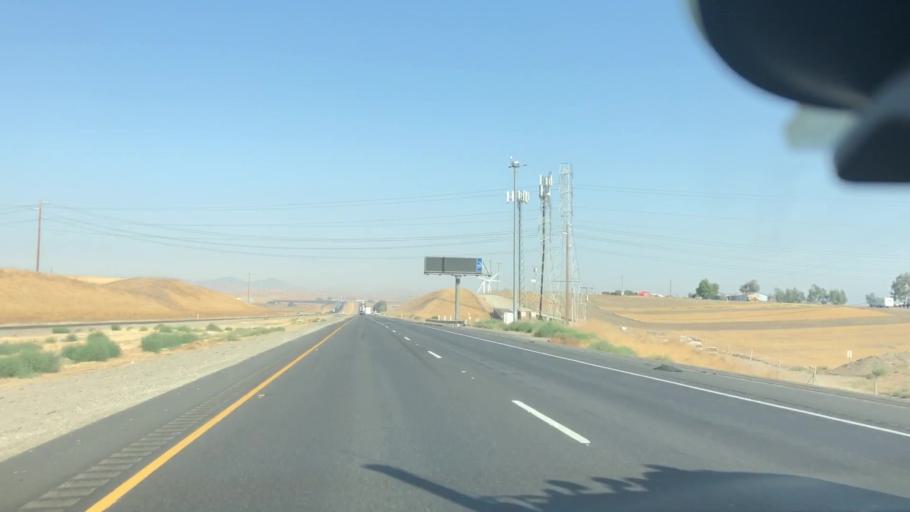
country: US
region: California
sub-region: San Joaquin County
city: Mountain House
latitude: 37.7037
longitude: -121.5090
